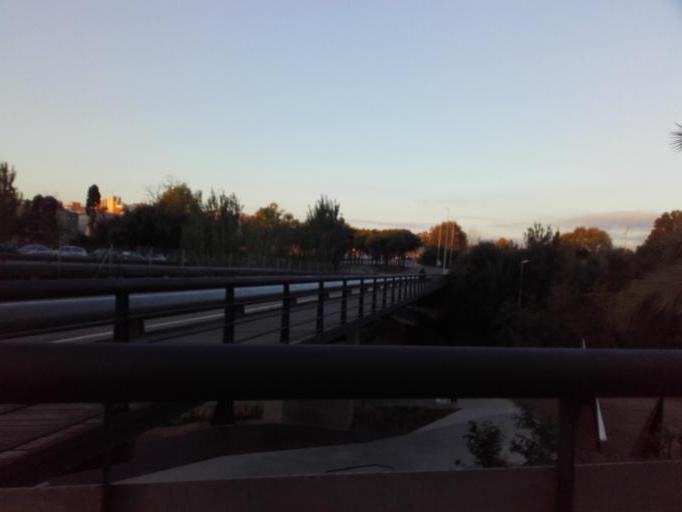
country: ES
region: Catalonia
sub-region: Provincia de Barcelona
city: L'Hospitalet de Llobregat
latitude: 41.3775
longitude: 2.1095
